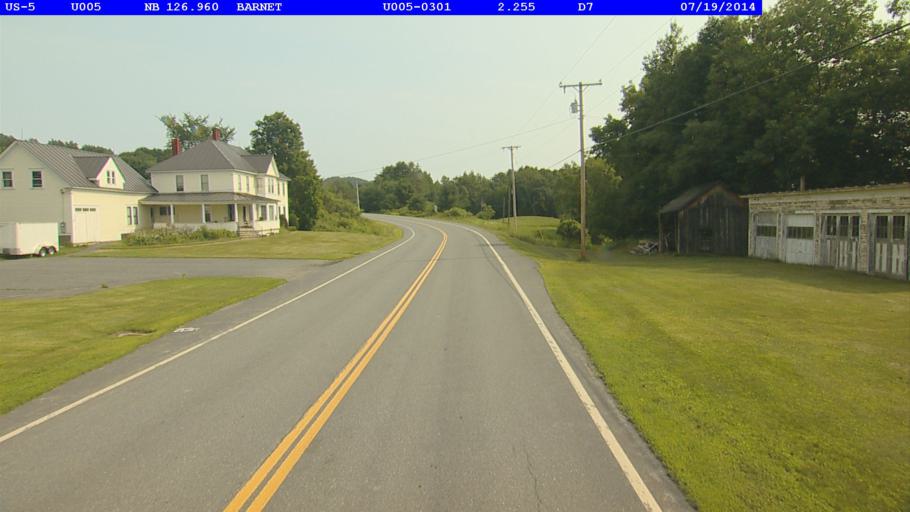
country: US
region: New Hampshire
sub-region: Grafton County
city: Woodsville
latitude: 44.2857
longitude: -72.0604
